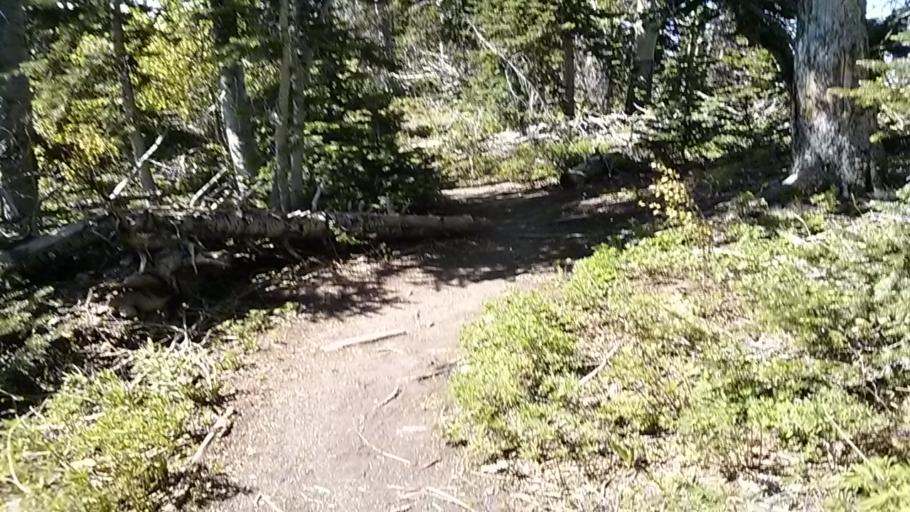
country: US
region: Utah
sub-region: Iron County
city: Parowan
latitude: 37.6388
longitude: -112.8230
